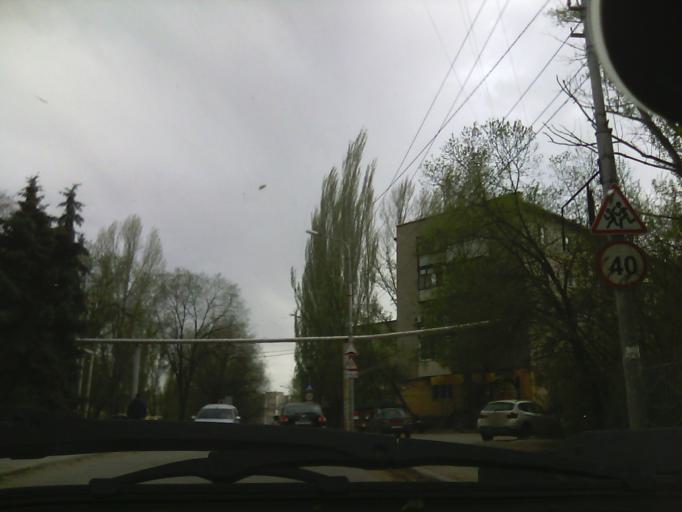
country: RU
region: Saratov
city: Sokolovyy
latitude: 51.5993
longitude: 45.9236
